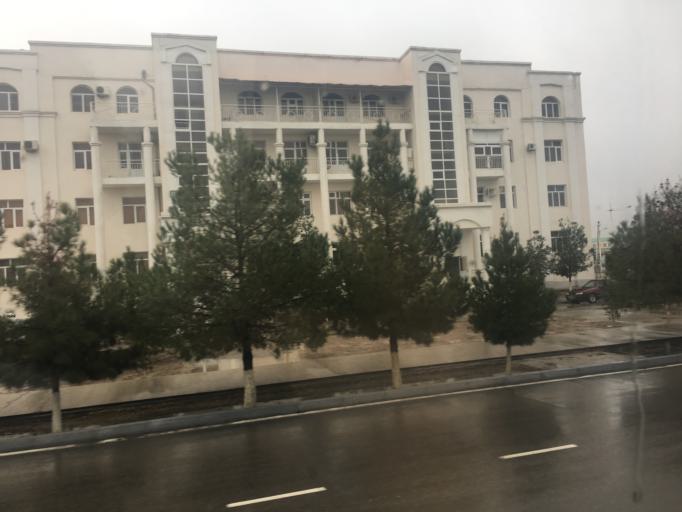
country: TM
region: Lebap
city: Turkmenabat
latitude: 39.0966
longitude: 63.5952
